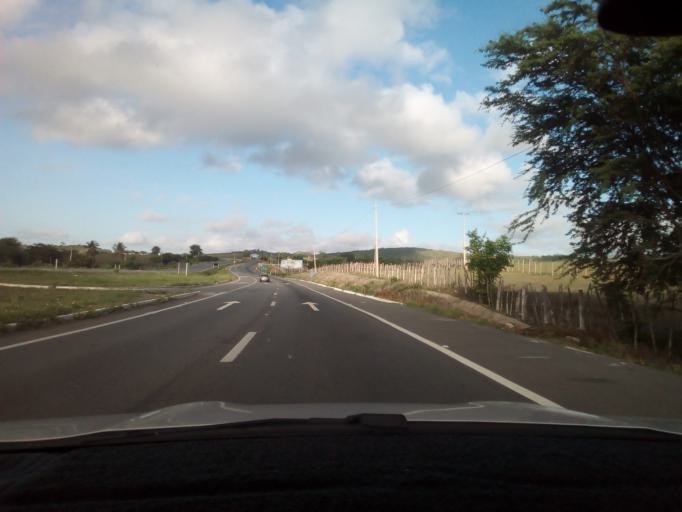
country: BR
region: Paraiba
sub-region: Inga
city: Inga
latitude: -7.2142
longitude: -35.5894
